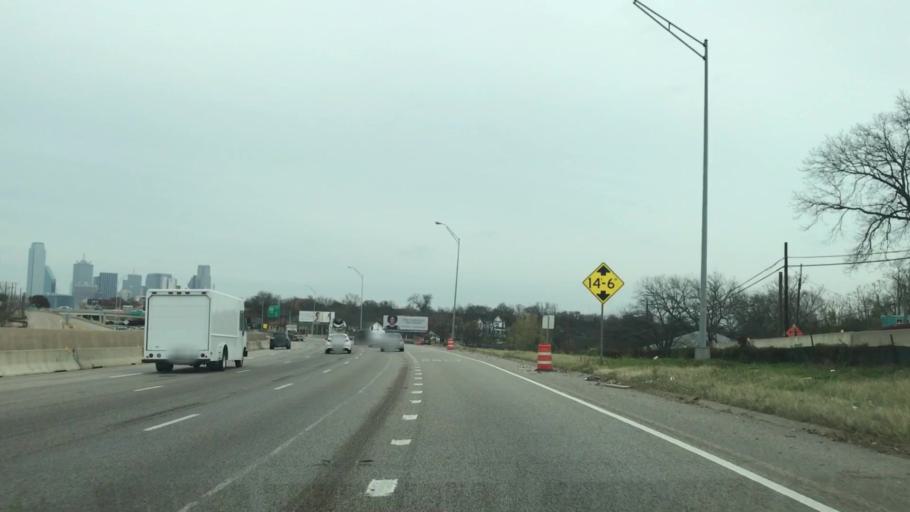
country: US
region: Texas
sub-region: Dallas County
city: Dallas
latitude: 32.7469
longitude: -96.8105
